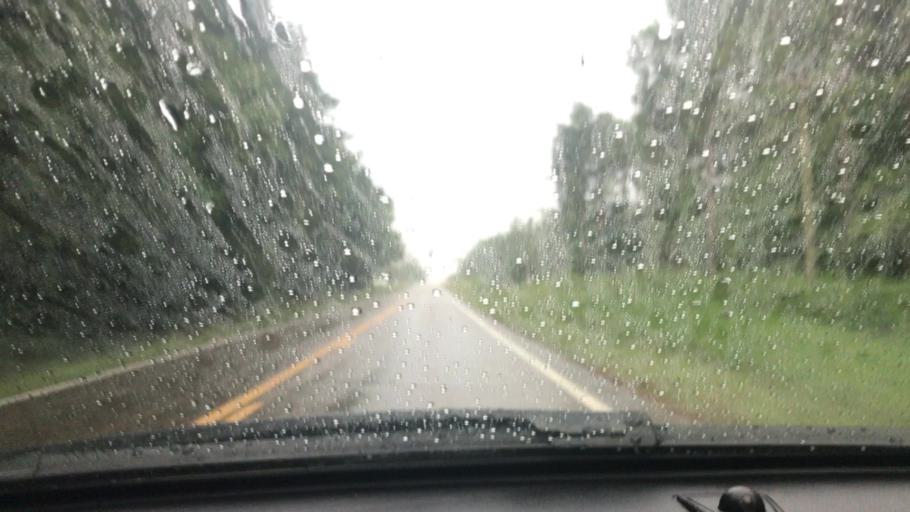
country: US
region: Mississippi
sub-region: Pike County
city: Summit
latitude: 31.3145
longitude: -90.5241
